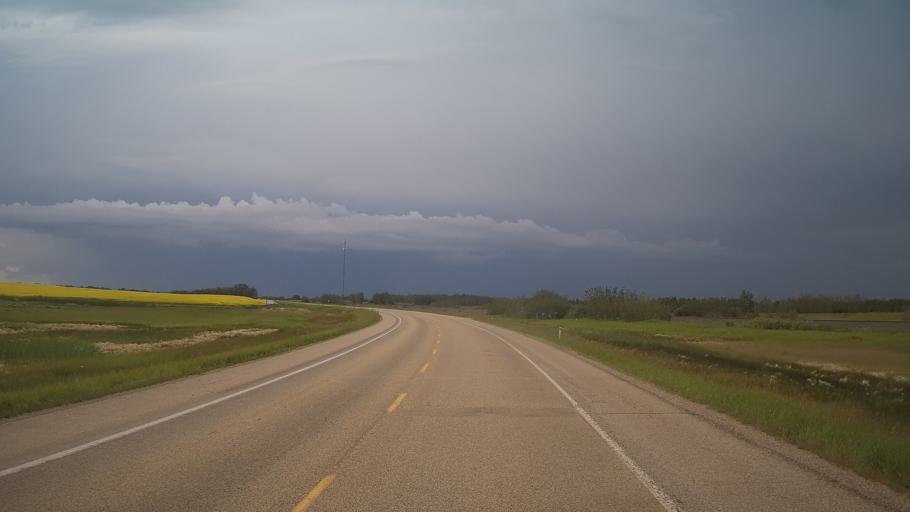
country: CA
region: Alberta
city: Vegreville
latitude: 53.2336
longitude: -112.2500
